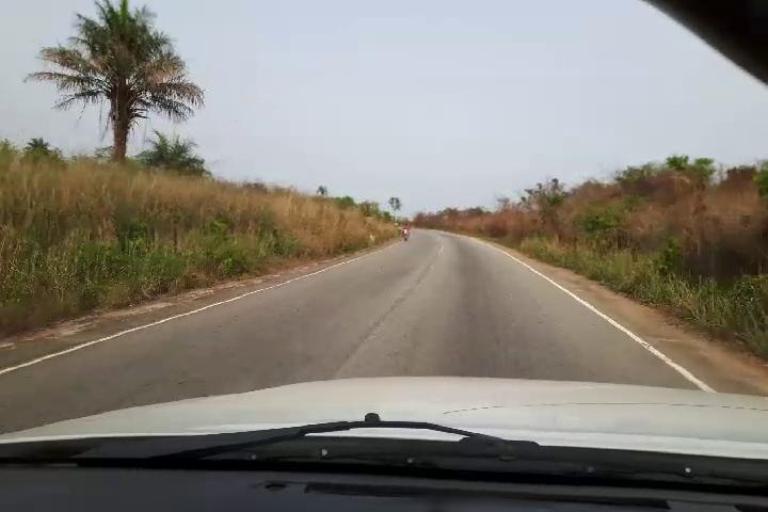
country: SL
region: Southern Province
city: Baoma
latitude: 7.9263
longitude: -11.5867
